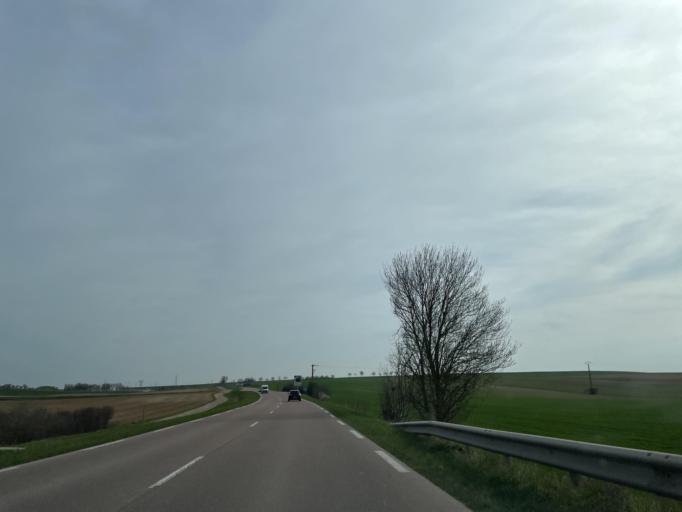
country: FR
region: Champagne-Ardenne
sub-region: Departement de l'Aube
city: Nogent-sur-Seine
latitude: 48.4823
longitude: 3.5015
